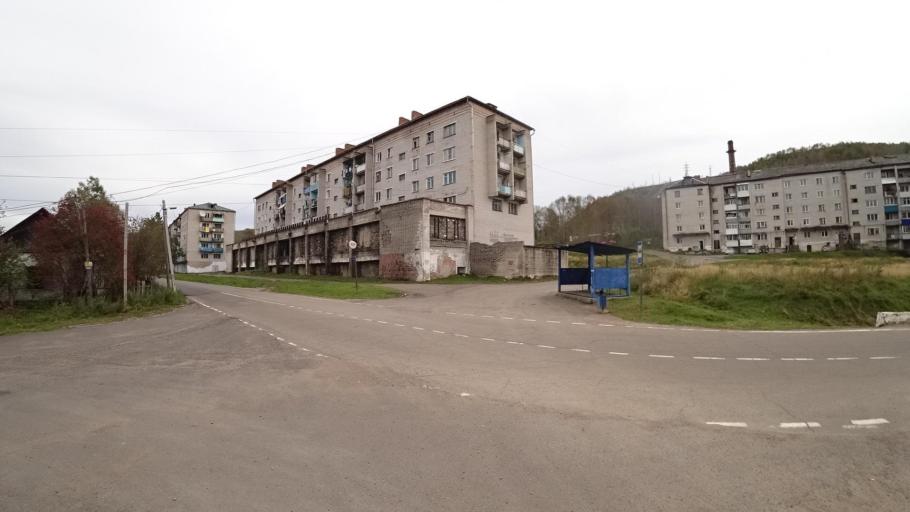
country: RU
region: Jewish Autonomous Oblast
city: Khingansk
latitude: 49.1258
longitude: 131.1898
